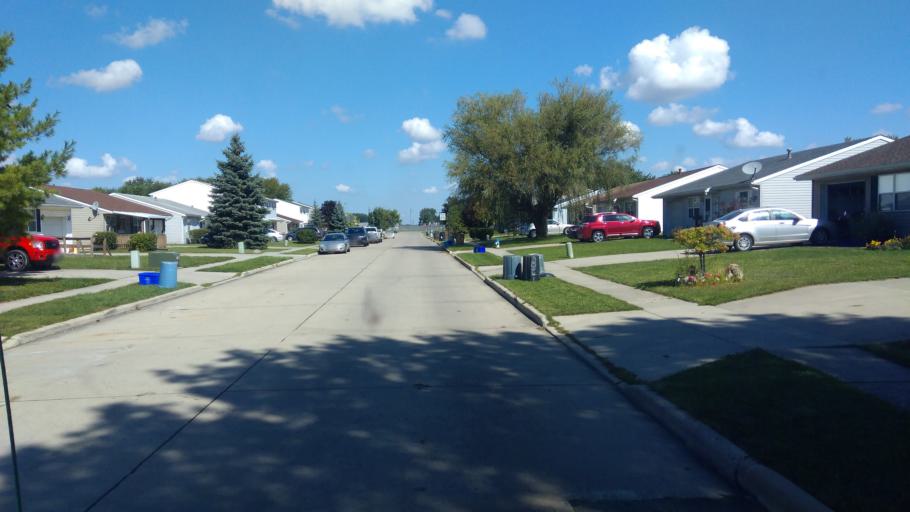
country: US
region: Ohio
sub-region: Marion County
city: Marion
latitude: 40.6123
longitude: -83.1125
